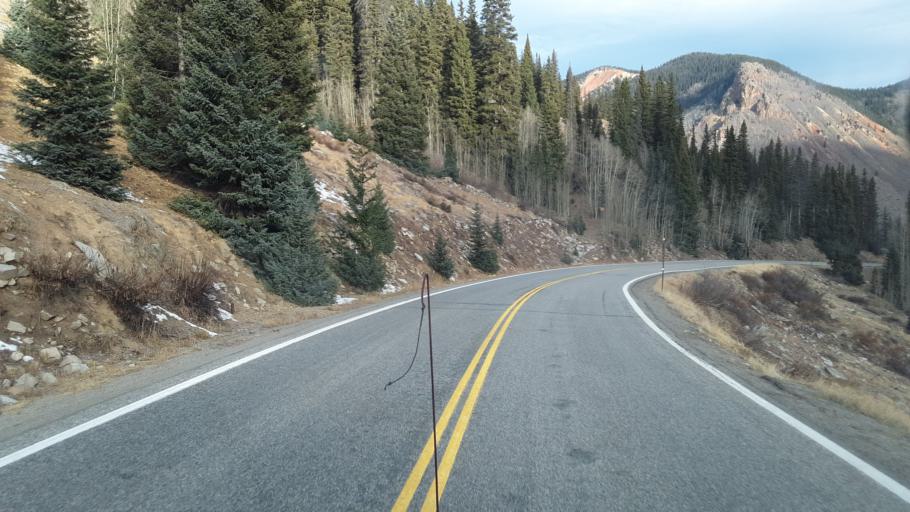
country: US
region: Colorado
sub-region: San Juan County
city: Silverton
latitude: 37.7954
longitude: -107.6739
